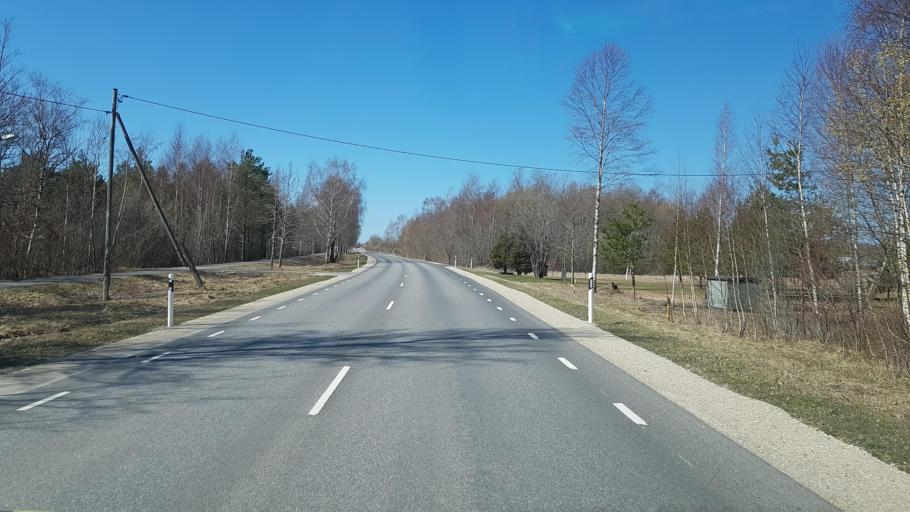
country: EE
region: Saare
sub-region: Kuressaare linn
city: Kuressaare
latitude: 58.2561
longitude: 22.5398
